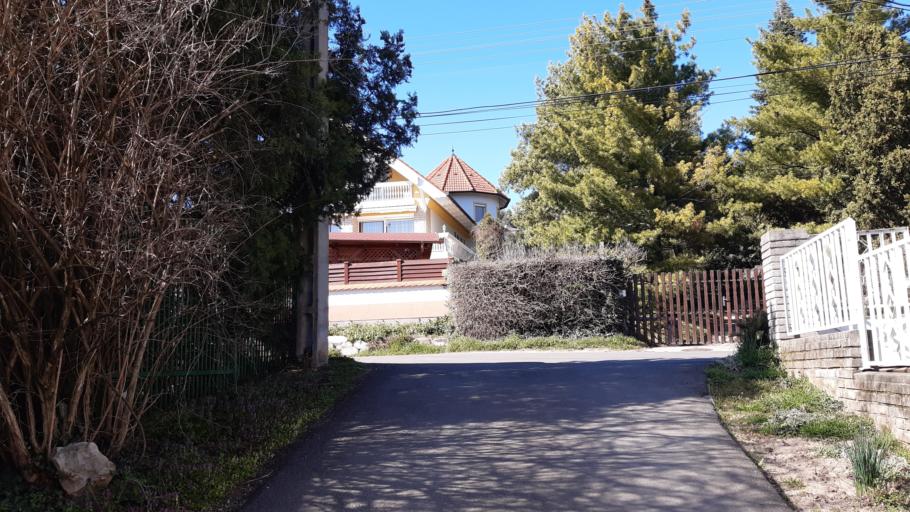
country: HU
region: Baranya
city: Pecs
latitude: 46.0706
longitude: 18.1962
